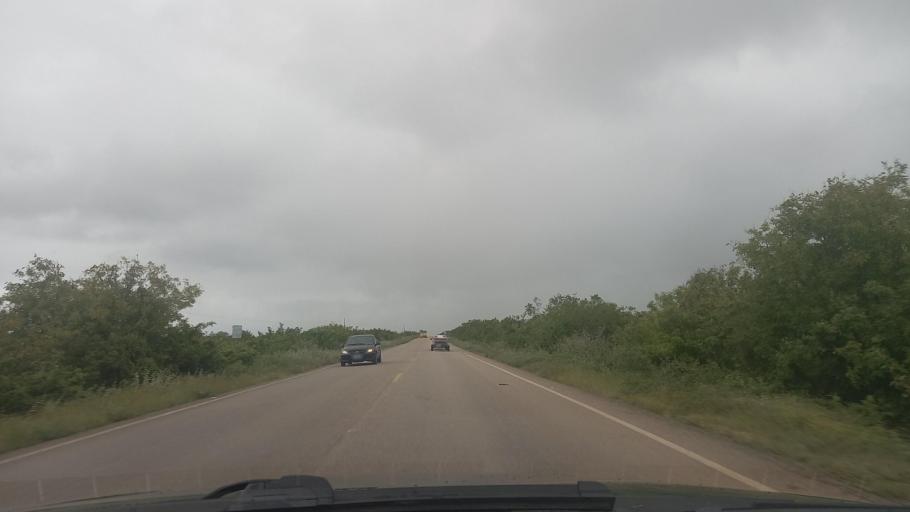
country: BR
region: Bahia
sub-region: Paulo Afonso
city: Paulo Afonso
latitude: -9.3365
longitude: -38.2843
